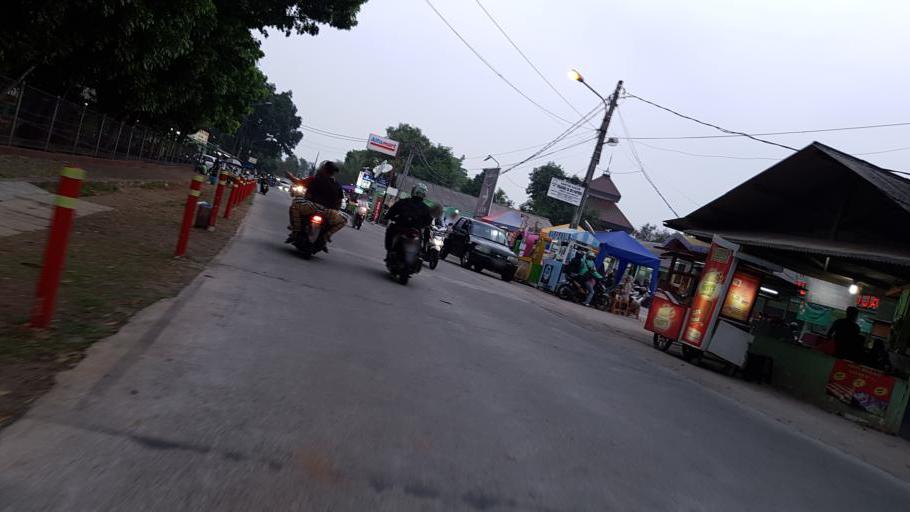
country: ID
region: West Java
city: Depok
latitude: -6.3408
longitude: 106.8436
